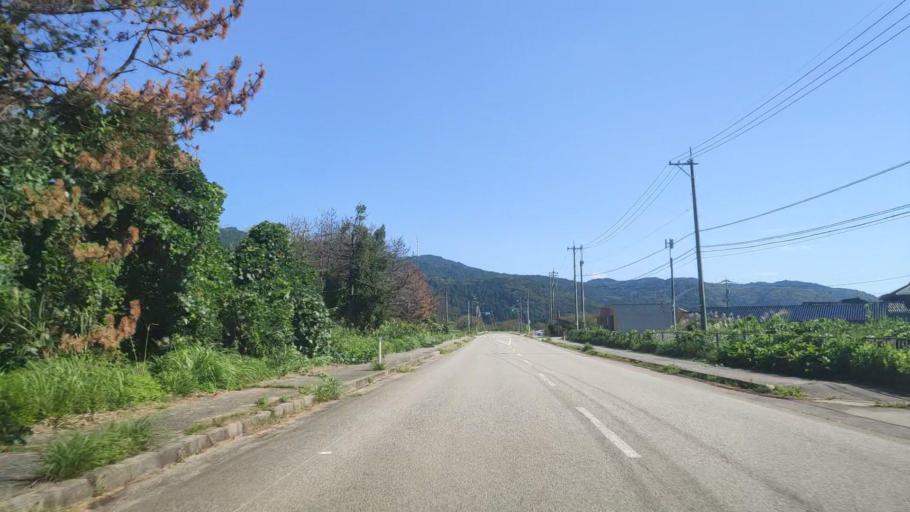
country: JP
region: Ishikawa
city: Nanao
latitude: 37.2897
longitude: 136.7405
